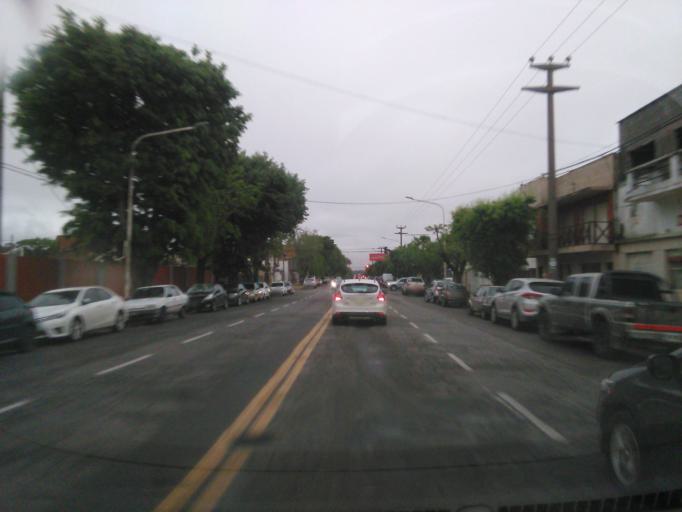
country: AR
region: Buenos Aires
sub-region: Partido de Tandil
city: Tandil
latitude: -37.3327
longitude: -59.1431
